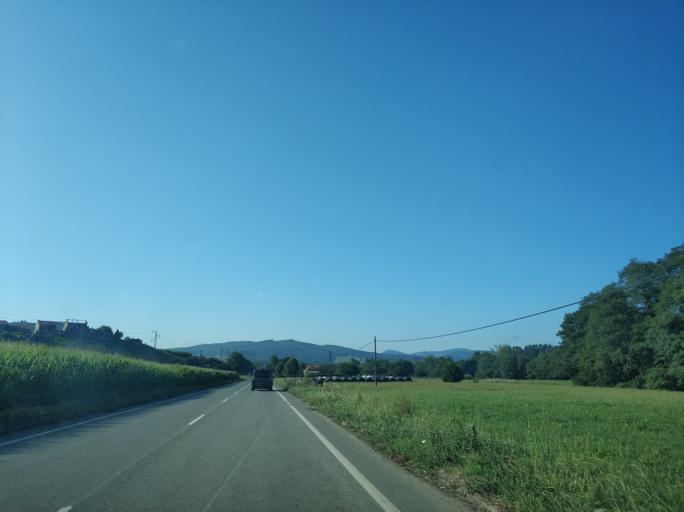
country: ES
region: Cantabria
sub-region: Provincia de Cantabria
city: Polanco
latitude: 43.3762
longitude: -3.9640
